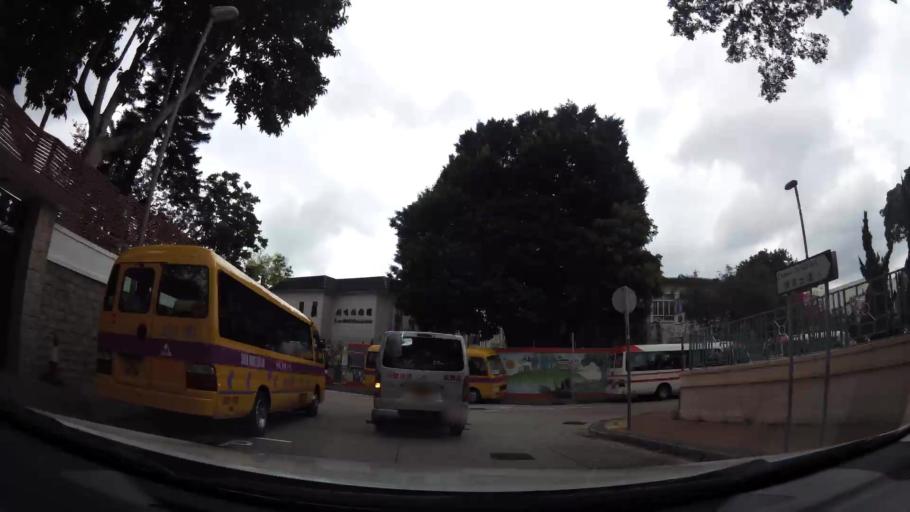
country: HK
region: Kowloon City
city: Kowloon
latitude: 22.3283
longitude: 114.1772
